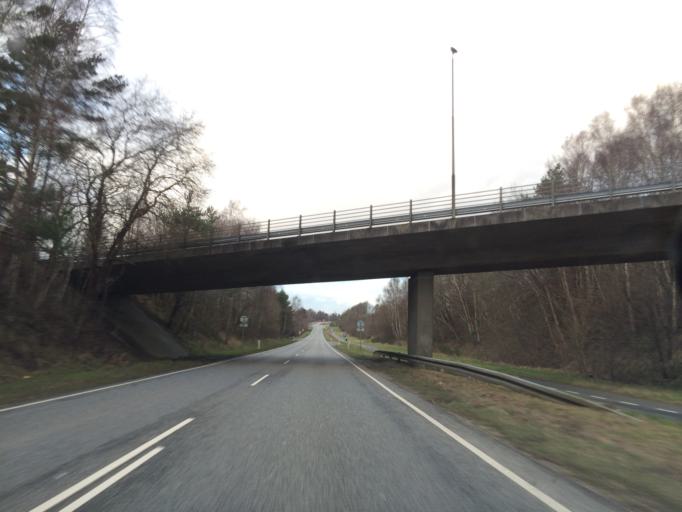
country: DK
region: Central Jutland
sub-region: Silkeborg Kommune
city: Virklund
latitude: 56.1263
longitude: 9.5655
